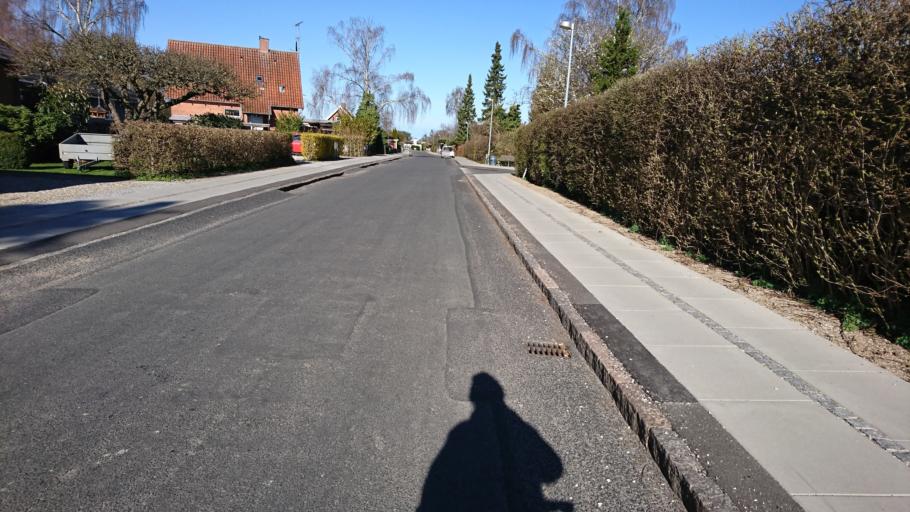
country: DK
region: Capital Region
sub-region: Ballerup Kommune
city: Ballerup
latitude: 55.7239
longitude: 12.4002
